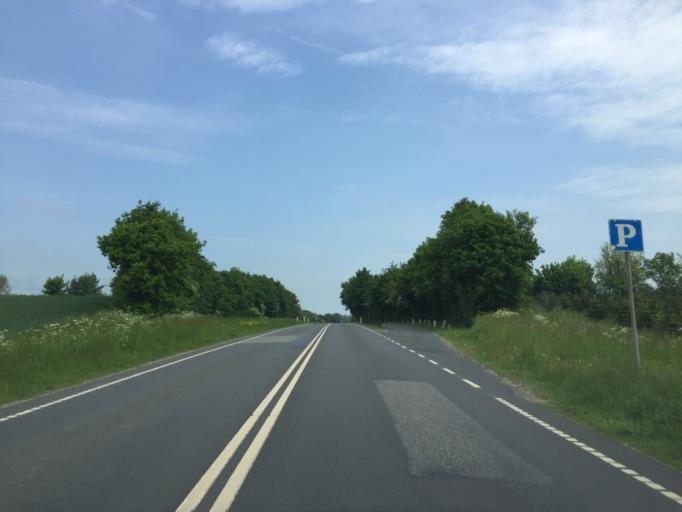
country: DK
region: South Denmark
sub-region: Svendborg Kommune
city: Thuro By
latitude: 55.1473
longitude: 10.7379
